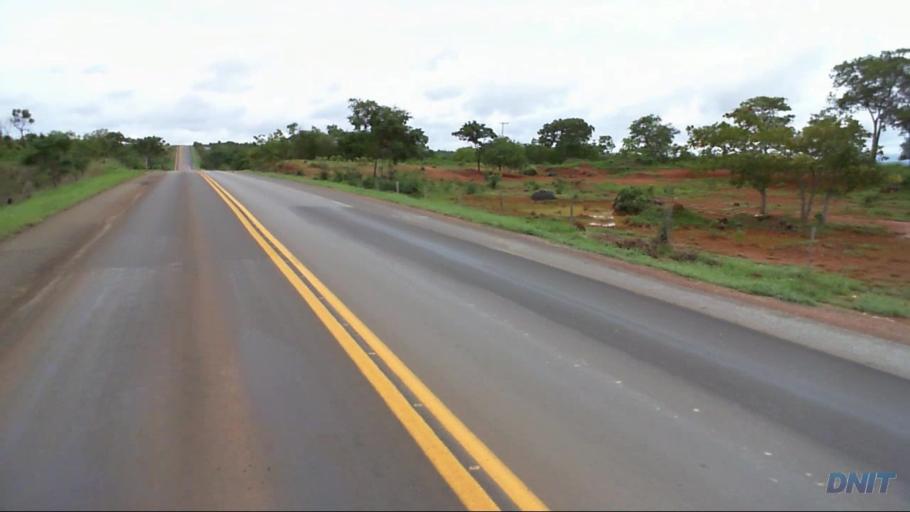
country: BR
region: Goias
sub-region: Padre Bernardo
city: Padre Bernardo
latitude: -15.1541
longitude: -48.3286
